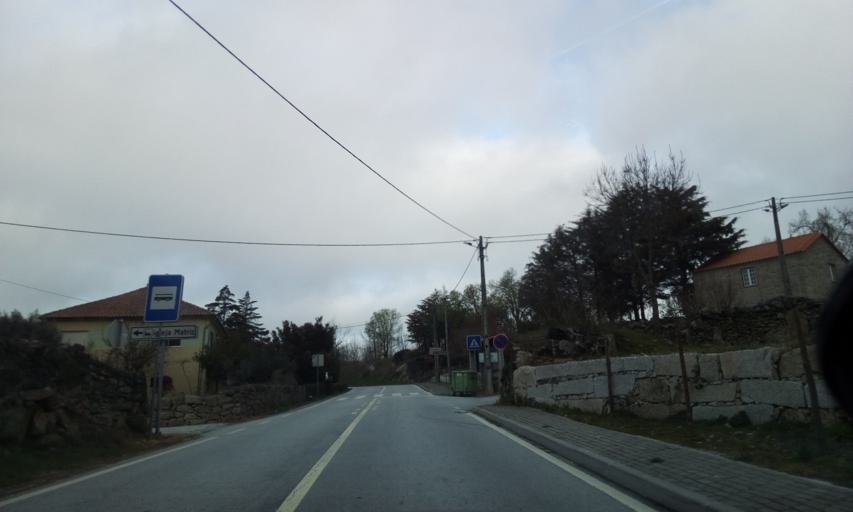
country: PT
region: Guarda
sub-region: Fornos de Algodres
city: Fornos de Algodres
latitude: 40.6558
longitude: -7.4832
